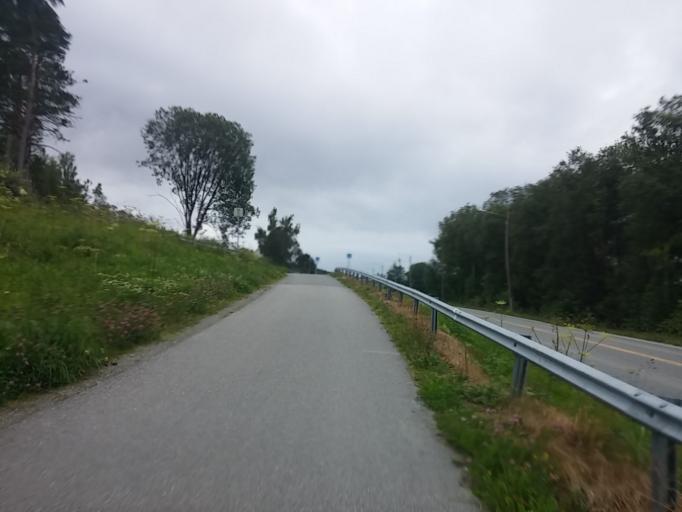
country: NO
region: Sor-Trondelag
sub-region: Malvik
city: Malvik
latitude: 63.4339
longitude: 10.6923
